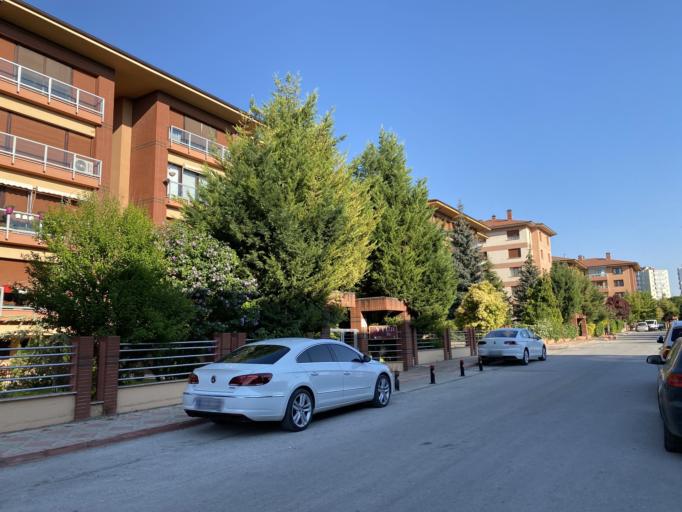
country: TR
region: Eskisehir
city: Eskisehir
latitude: 39.7628
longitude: 30.4962
